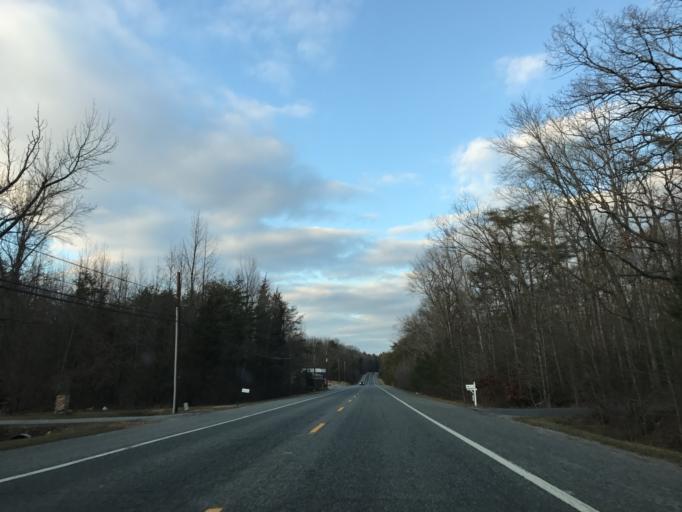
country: US
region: Maryland
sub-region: Cecil County
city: Charlestown
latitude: 39.5338
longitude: -75.9524
